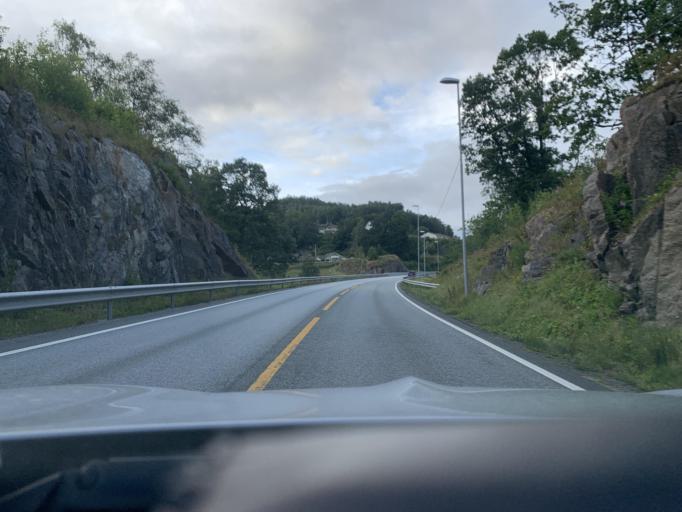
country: NO
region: Rogaland
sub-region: Bjerkreim
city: Vikesa
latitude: 58.5803
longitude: 6.0633
